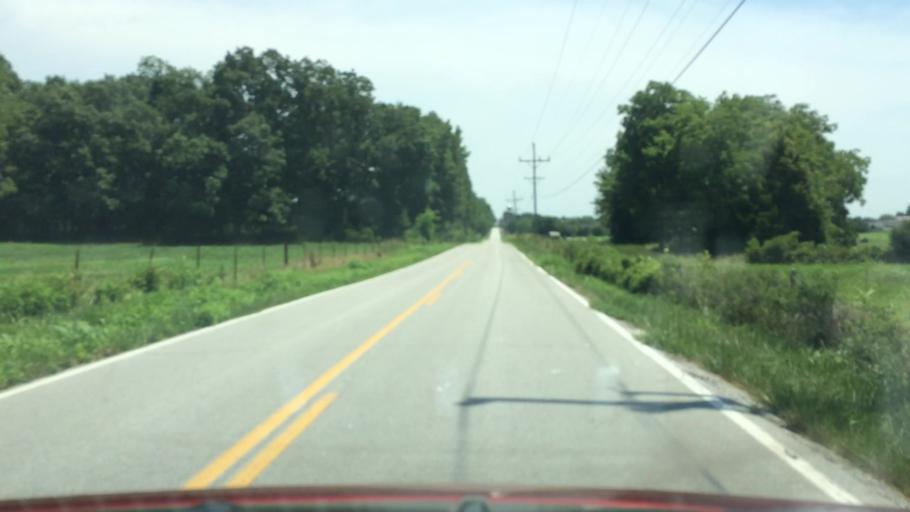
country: US
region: Missouri
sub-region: Greene County
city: Strafford
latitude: 37.2711
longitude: -93.1421
